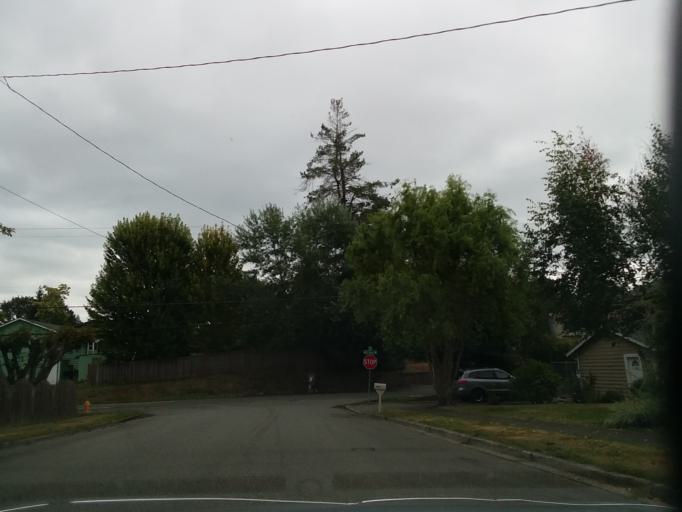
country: US
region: Washington
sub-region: Snohomish County
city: Alderwood Manor
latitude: 47.8248
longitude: -122.2877
